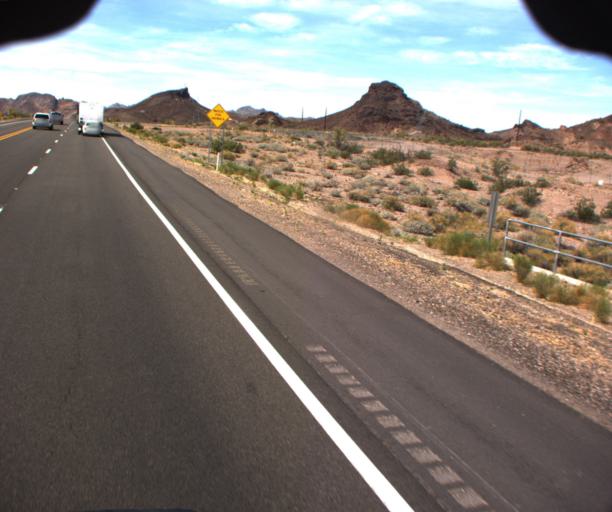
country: US
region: Arizona
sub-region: Mohave County
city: Desert Hills
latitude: 34.5825
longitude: -114.3680
